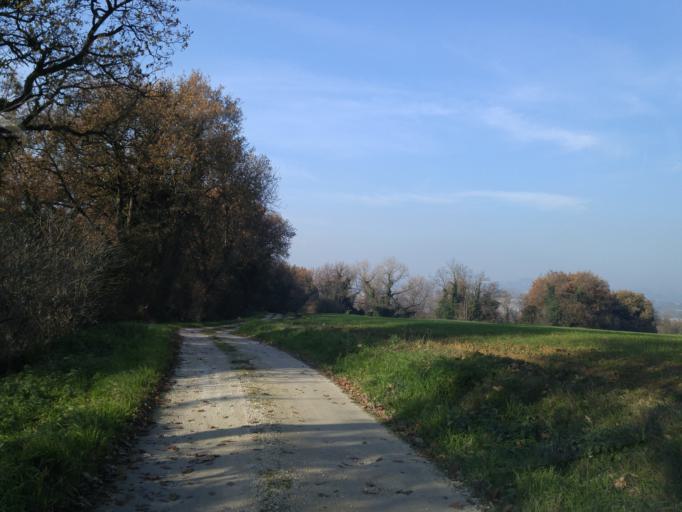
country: IT
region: The Marches
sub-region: Provincia di Pesaro e Urbino
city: Tavernelle
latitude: 43.7093
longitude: 12.8912
